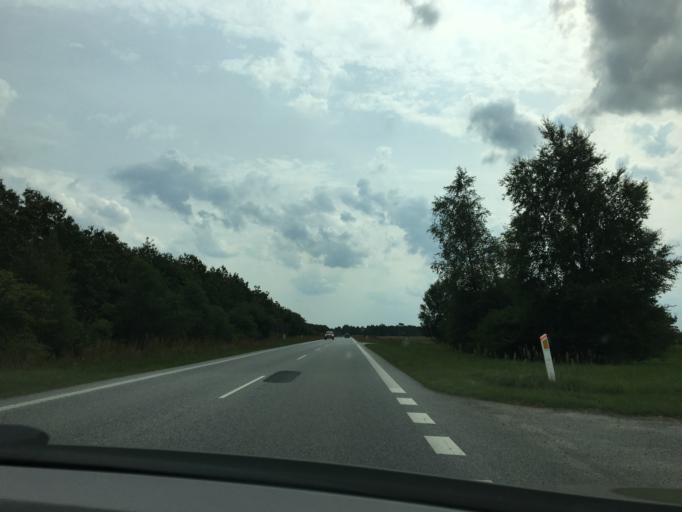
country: DK
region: Central Jutland
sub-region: Skive Kommune
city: Skive
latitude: 56.5326
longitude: 9.0380
